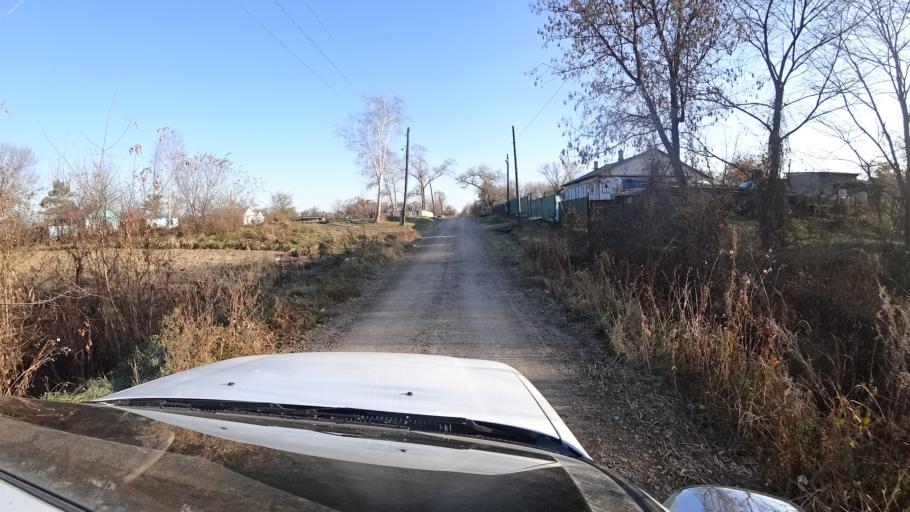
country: RU
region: Primorskiy
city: Lazo
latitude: 45.8720
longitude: 133.6447
